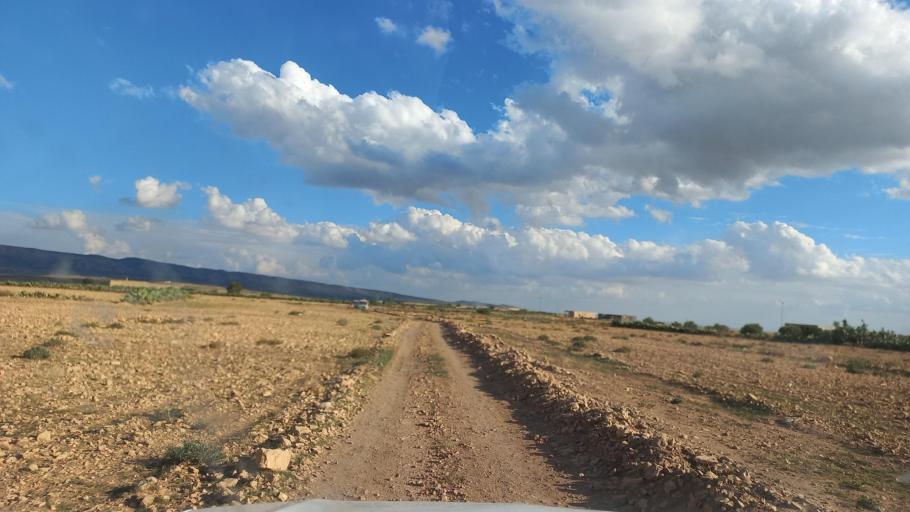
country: TN
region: Al Qasrayn
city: Sbiba
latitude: 35.3855
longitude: 9.0685
